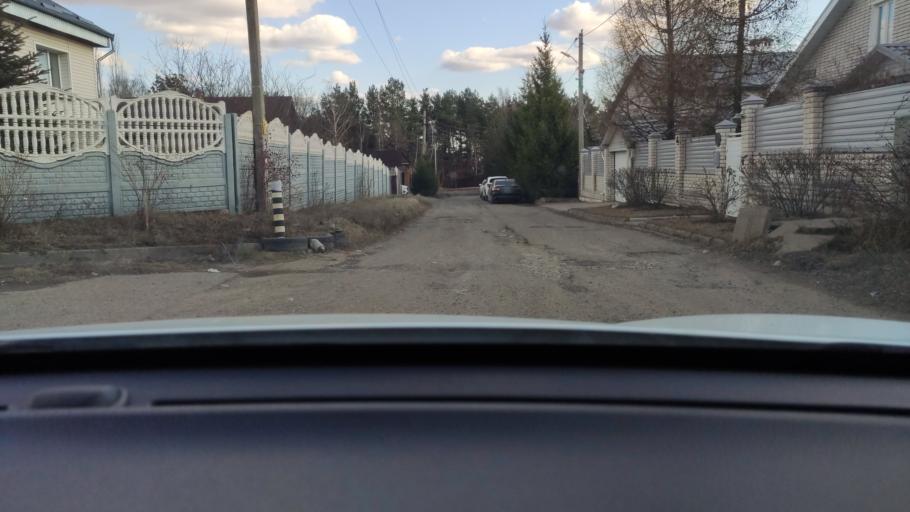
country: RU
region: Tatarstan
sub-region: Gorod Kazan'
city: Kazan
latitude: 55.8089
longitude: 49.2204
